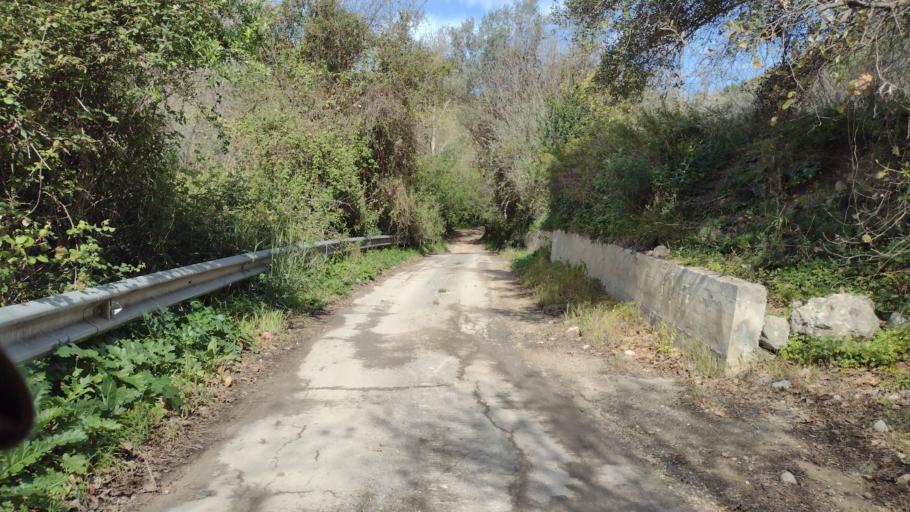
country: IT
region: Sicily
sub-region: Provincia di Siracusa
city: Noto
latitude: 36.9083
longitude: 15.0174
